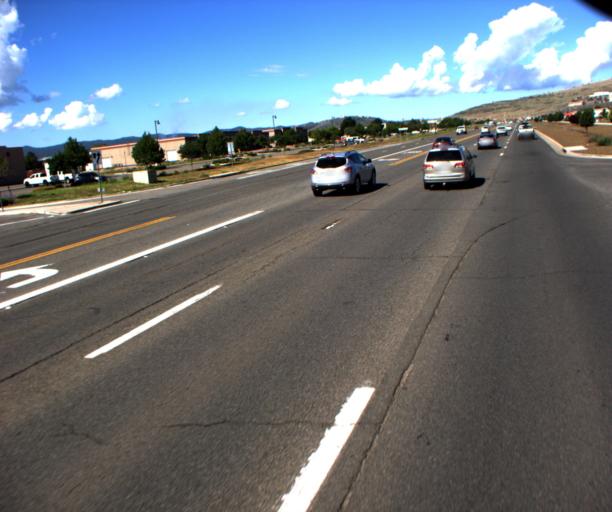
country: US
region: Arizona
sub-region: Yavapai County
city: Prescott Valley
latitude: 34.5821
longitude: -112.3481
